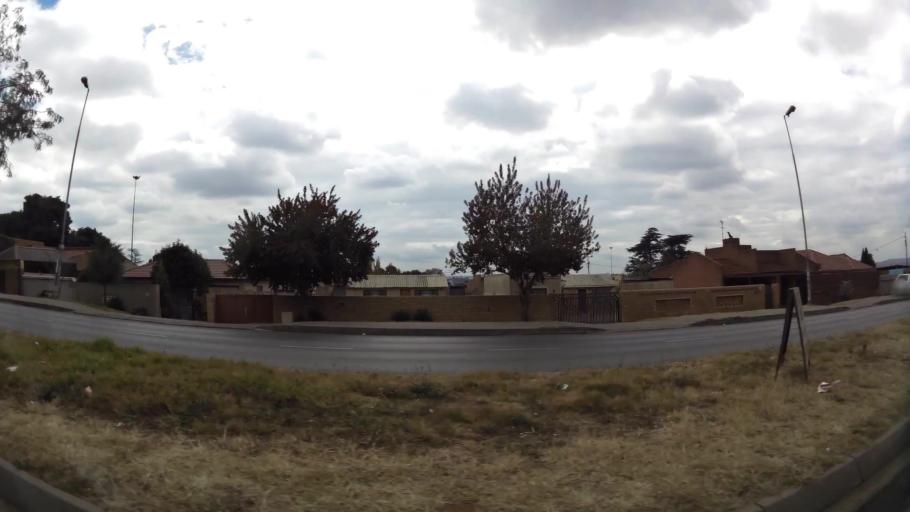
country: ZA
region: Gauteng
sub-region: City of Johannesburg Metropolitan Municipality
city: Soweto
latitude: -26.2684
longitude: 27.8708
